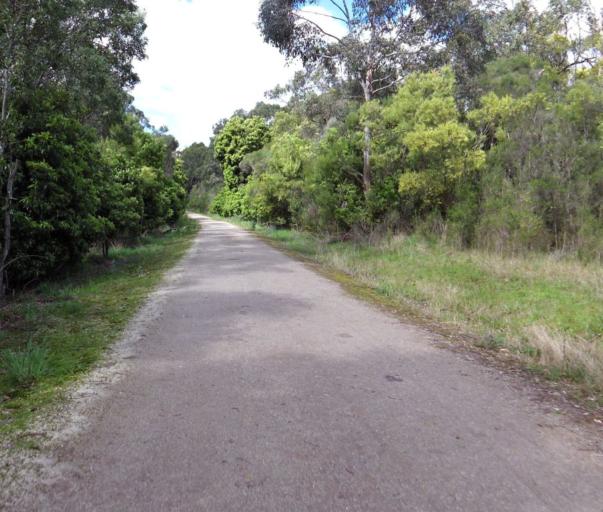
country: AU
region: Victoria
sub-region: Bass Coast
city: North Wonthaggi
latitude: -38.6757
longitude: 146.0328
